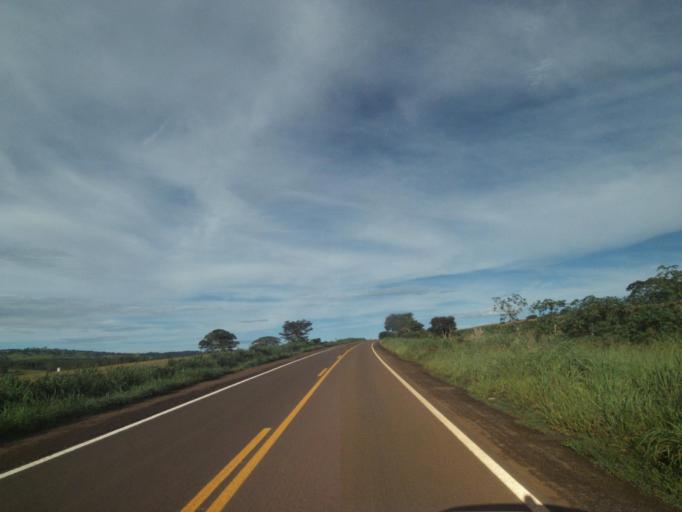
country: BR
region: Goias
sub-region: Jaragua
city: Jaragua
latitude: -15.9073
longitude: -49.5550
